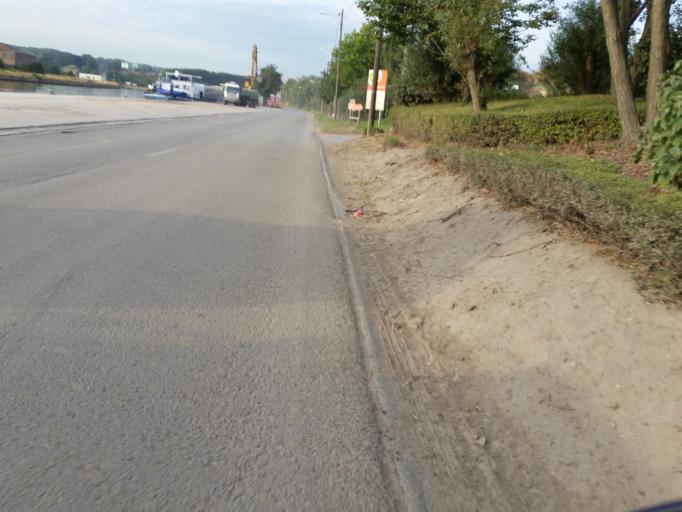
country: BE
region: Flanders
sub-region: Provincie Vlaams-Brabant
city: Vilvoorde
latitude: 50.9372
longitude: 4.4139
